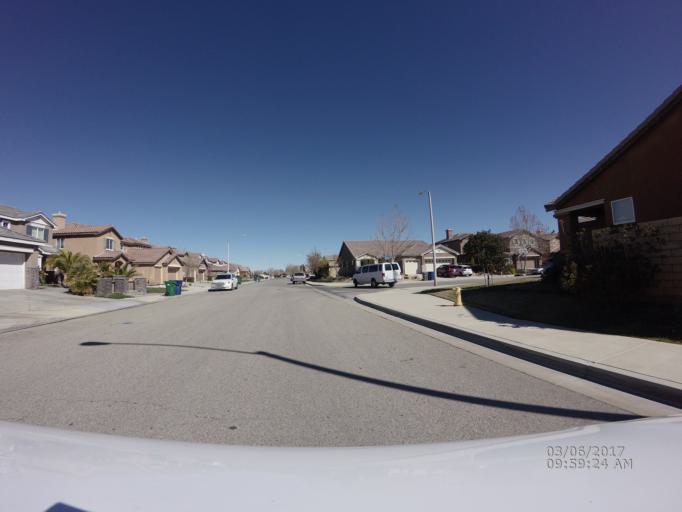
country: US
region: California
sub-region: Los Angeles County
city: Quartz Hill
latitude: 34.6502
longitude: -118.2047
